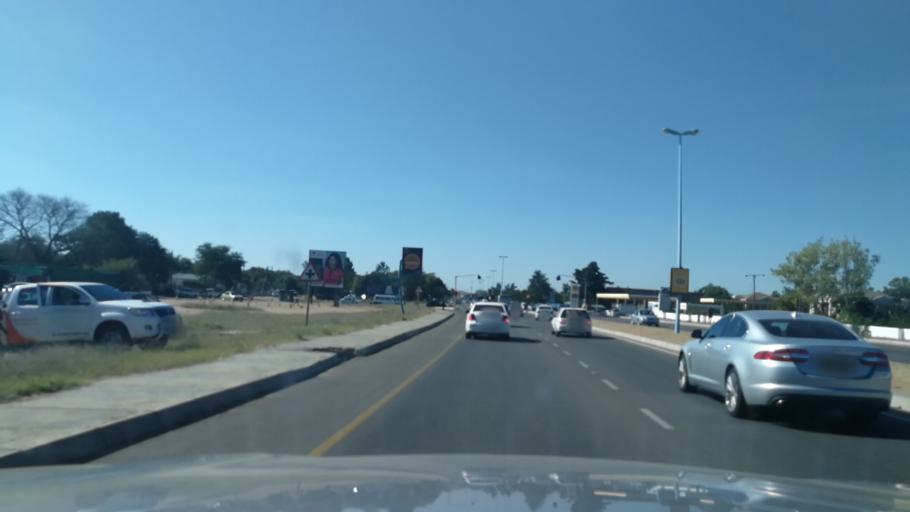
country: BW
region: South East
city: Gaborone
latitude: -24.6784
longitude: 25.9186
